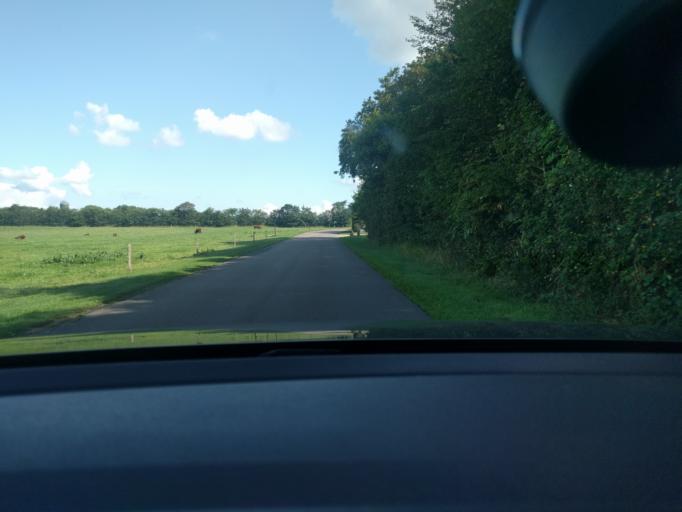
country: DK
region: Central Jutland
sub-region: Viborg Kommune
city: Stoholm
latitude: 56.4744
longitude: 9.2643
